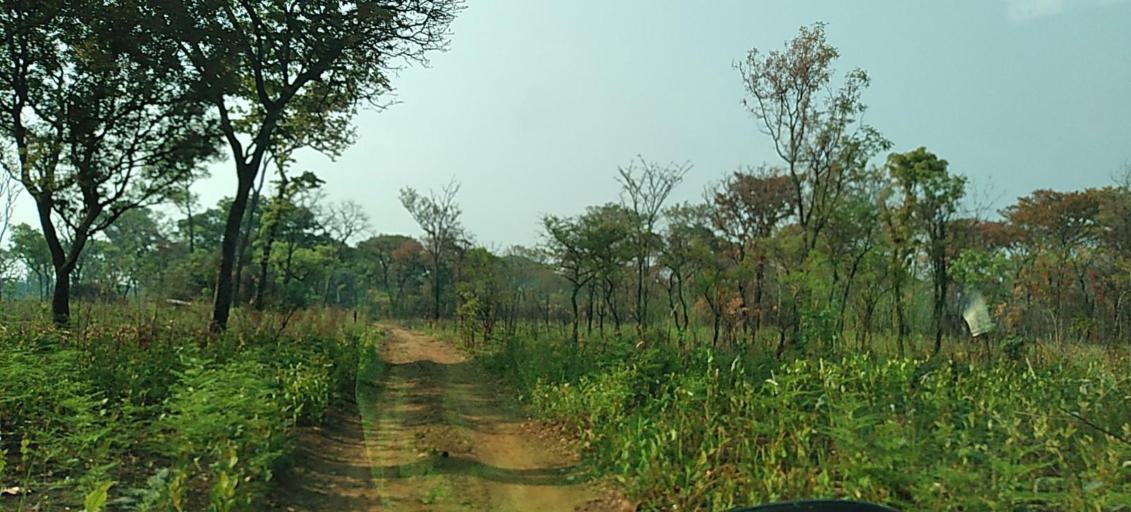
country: ZM
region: North-Western
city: Solwezi
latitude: -12.4050
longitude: 26.5870
